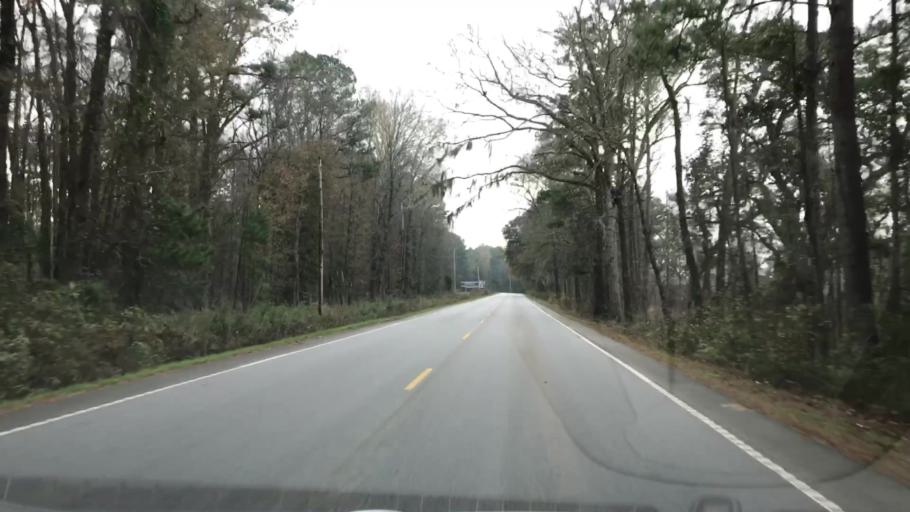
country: US
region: South Carolina
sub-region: Jasper County
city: Ridgeland
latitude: 32.5656
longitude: -80.9164
